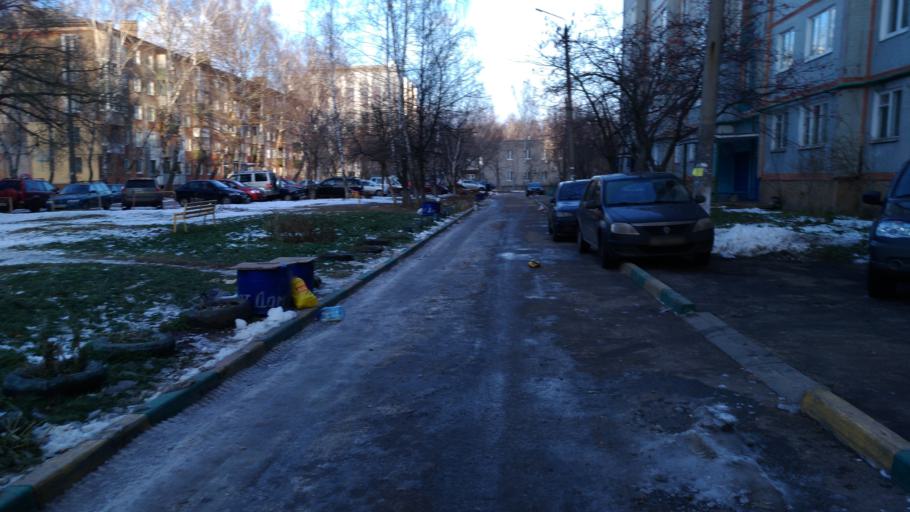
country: RU
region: Tula
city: Tula
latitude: 54.1933
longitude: 37.6894
